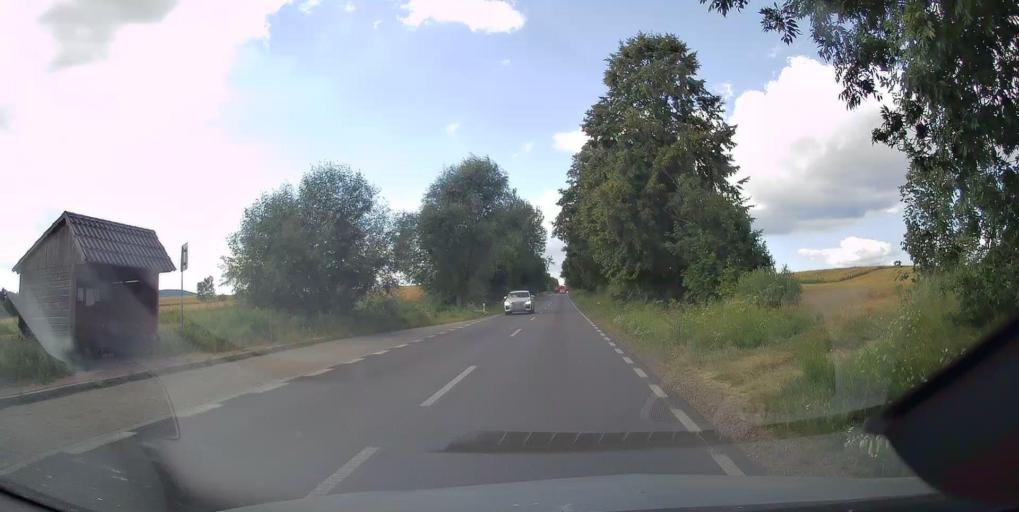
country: PL
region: Swietokrzyskie
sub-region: Powiat kielecki
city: Bodzentyn
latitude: 50.9200
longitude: 20.9905
